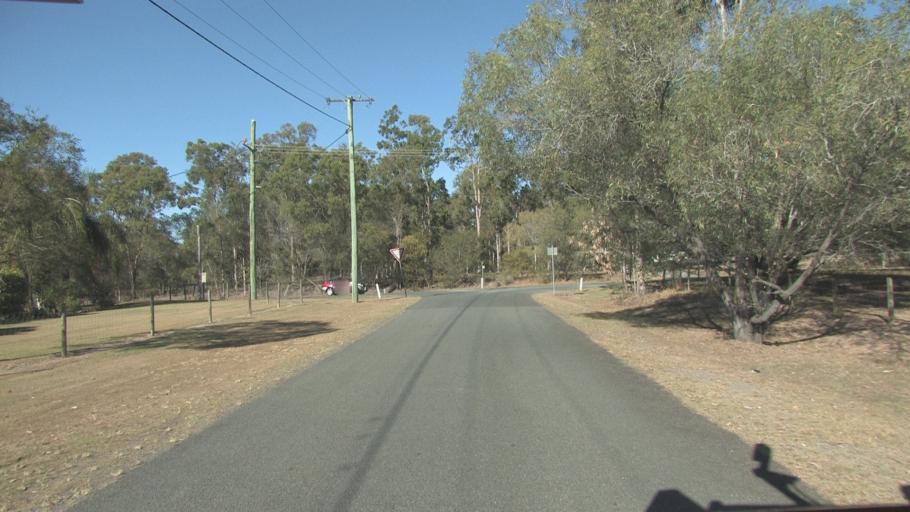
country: AU
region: Queensland
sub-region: Logan
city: North Maclean
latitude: -27.8099
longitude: 152.9885
